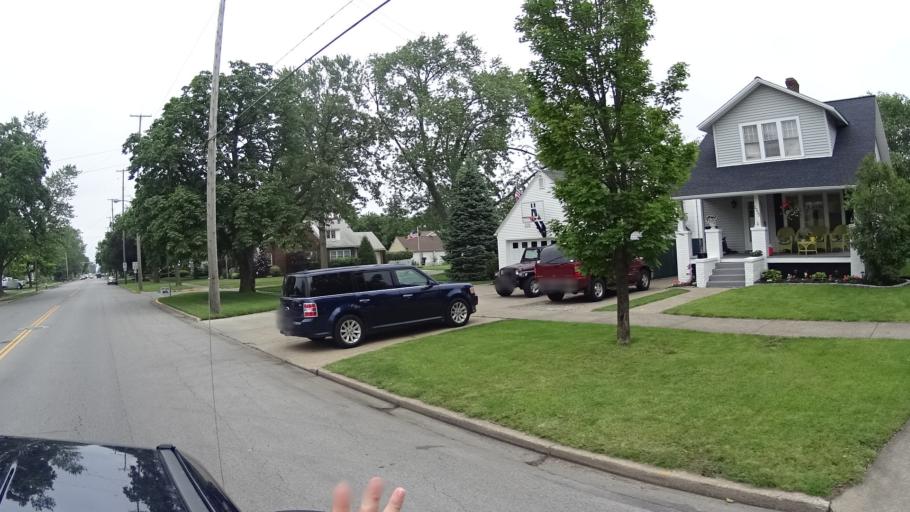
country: US
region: Ohio
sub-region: Erie County
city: Sandusky
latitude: 41.4341
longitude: -82.6987
